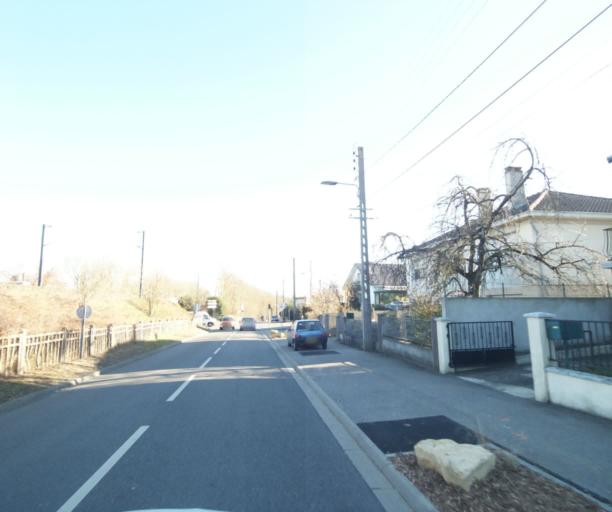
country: FR
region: Lorraine
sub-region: Departement de Meurthe-et-Moselle
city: Laneuveville-devant-Nancy
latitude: 48.6588
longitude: 6.2234
